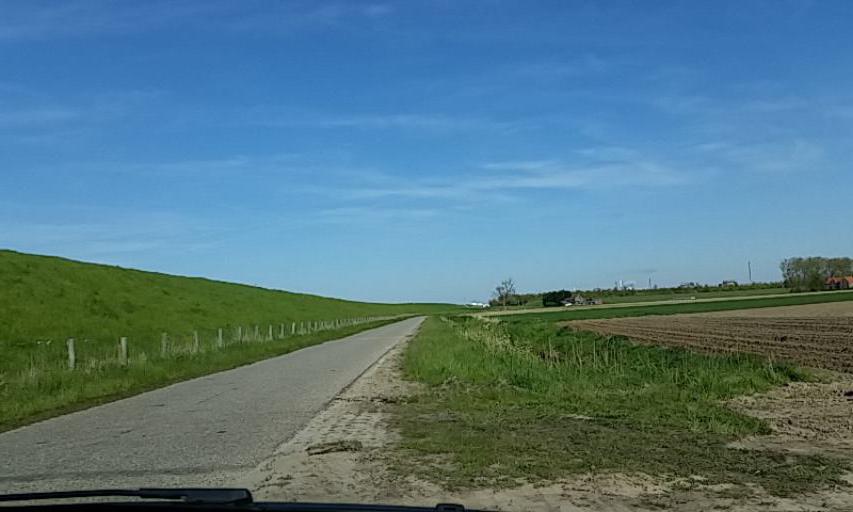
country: NL
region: Zeeland
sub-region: Gemeente Borsele
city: Borssele
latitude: 51.3480
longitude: 3.7207
